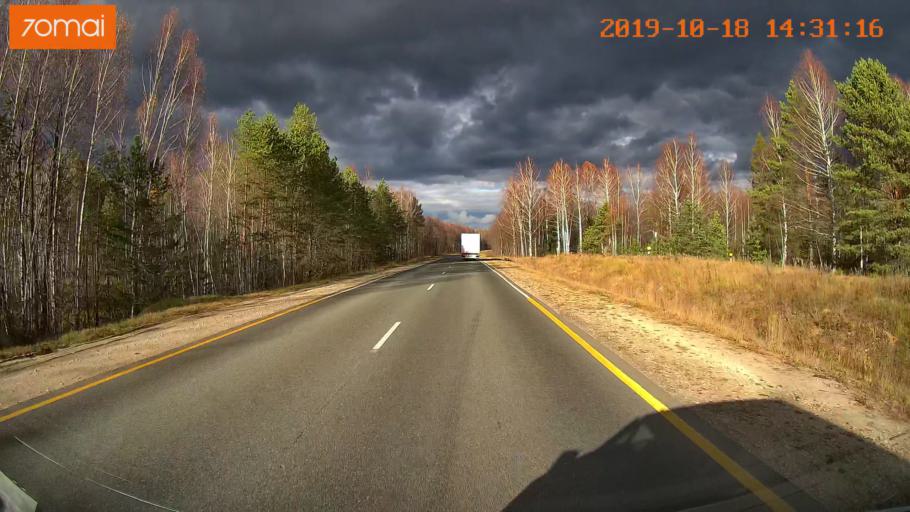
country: RU
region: Rjazan
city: Tuma
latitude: 55.1804
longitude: 40.5692
